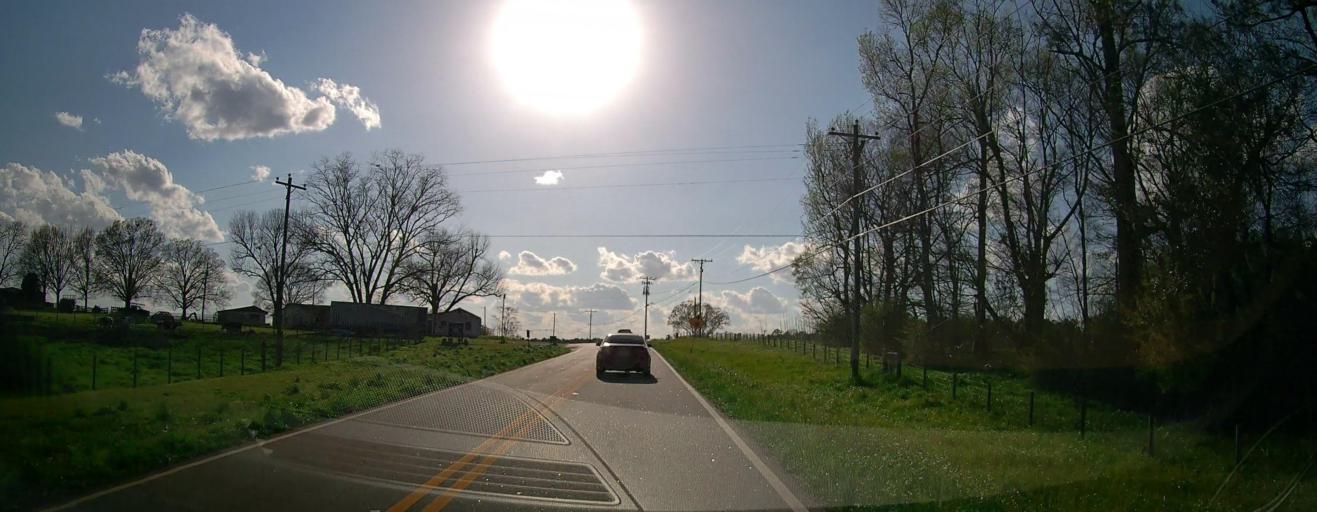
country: US
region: Georgia
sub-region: Putnam County
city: Eatonton
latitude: 33.1966
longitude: -83.4178
